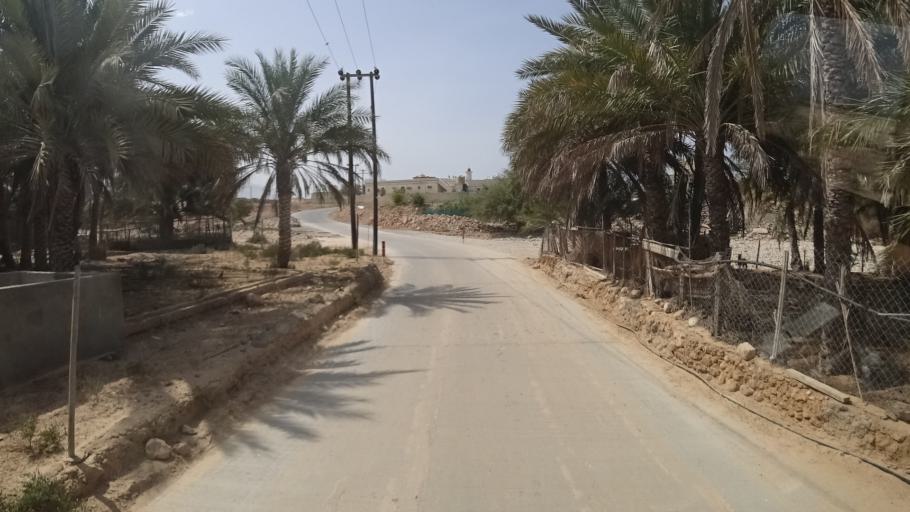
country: OM
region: Ash Sharqiyah
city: Sur
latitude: 22.9895
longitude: 59.1385
